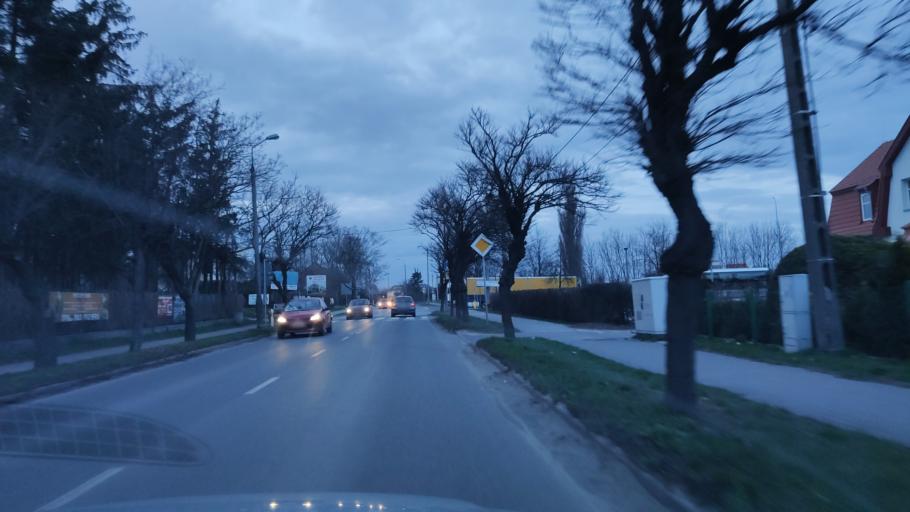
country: PL
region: Kujawsko-Pomorskie
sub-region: Powiat zninski
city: Znin
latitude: 52.8534
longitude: 17.7185
